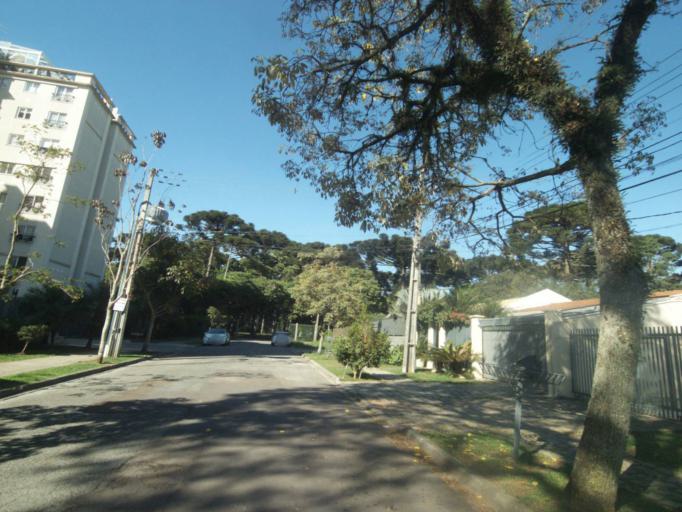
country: BR
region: Parana
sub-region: Curitiba
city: Curitiba
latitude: -25.3926
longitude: -49.2326
